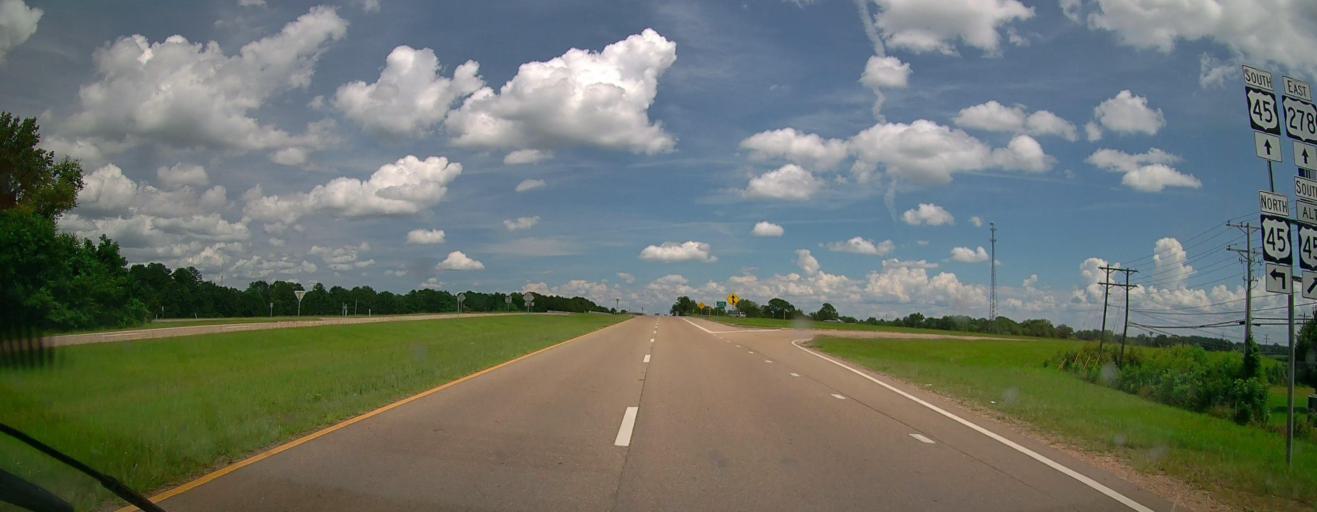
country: US
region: Mississippi
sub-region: Lee County
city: Shannon
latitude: 34.1180
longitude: -88.7047
